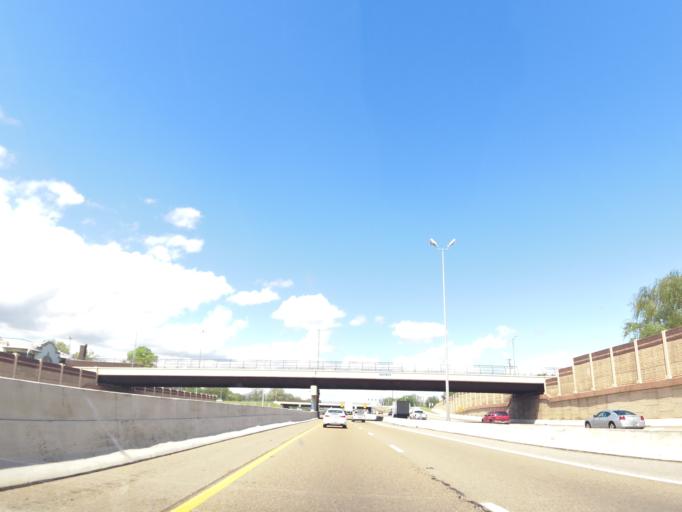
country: US
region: Tennessee
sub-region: Shelby County
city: Memphis
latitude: 35.1544
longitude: -90.0210
